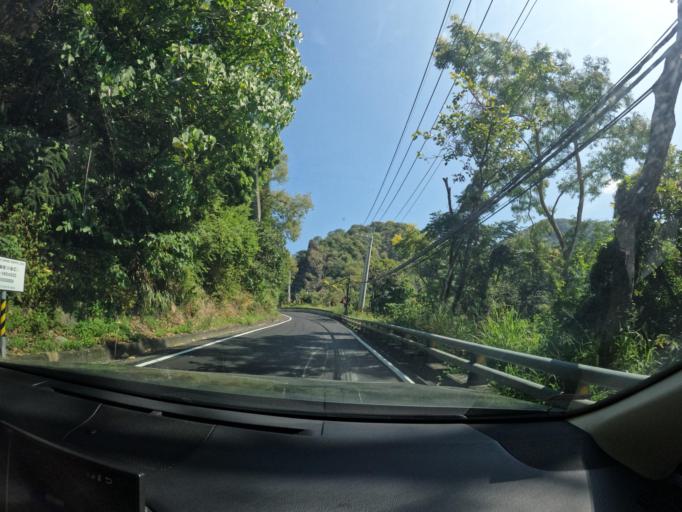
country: TW
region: Taiwan
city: Yujing
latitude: 23.1154
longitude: 120.7135
